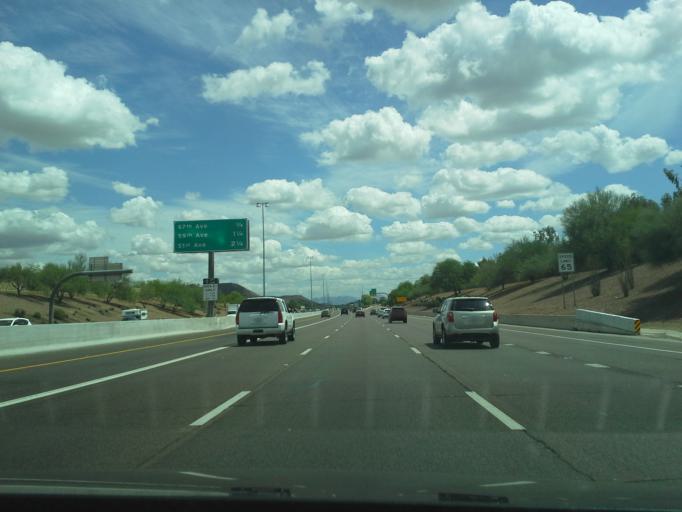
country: US
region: Arizona
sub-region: Maricopa County
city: Peoria
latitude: 33.6676
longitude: -112.2125
